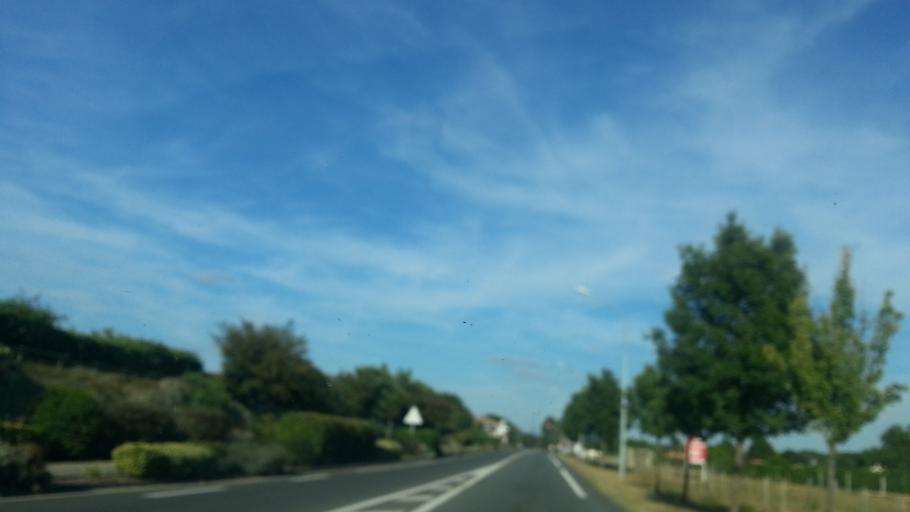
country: FR
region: Aquitaine
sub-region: Departement de la Gironde
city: Beautiran
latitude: 44.6990
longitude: -0.4642
